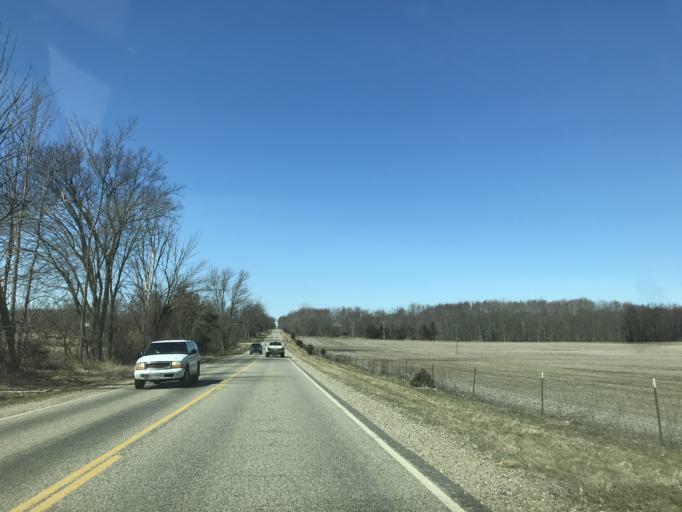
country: US
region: Michigan
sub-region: Hillsdale County
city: Litchfield
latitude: 41.9857
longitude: -84.8027
